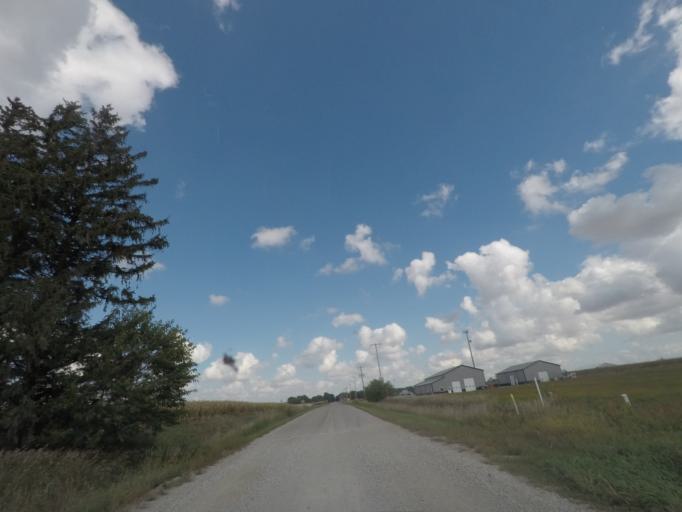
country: US
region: Iowa
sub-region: Story County
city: Nevada
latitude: 42.0042
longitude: -93.3192
